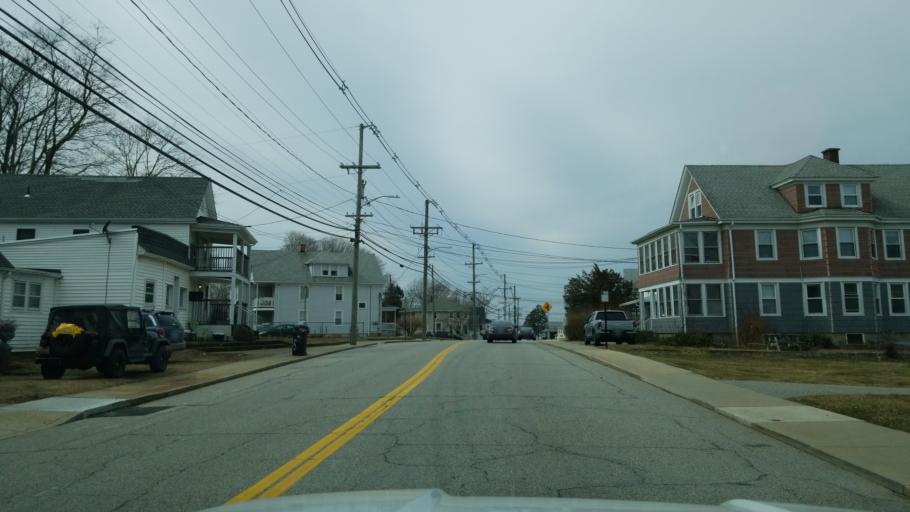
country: US
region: Connecticut
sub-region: New London County
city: Groton
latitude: 41.3465
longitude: -72.0723
